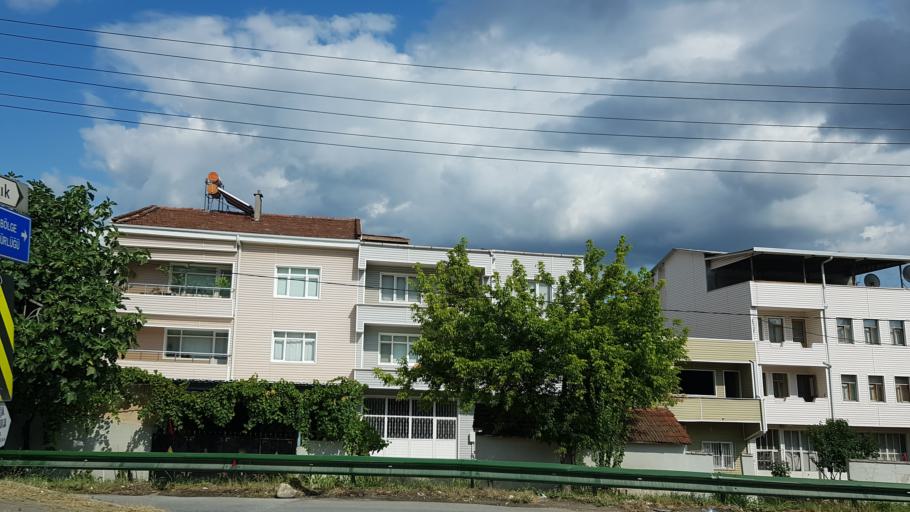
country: TR
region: Bursa
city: Demirtas
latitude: 40.2980
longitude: 29.0591
